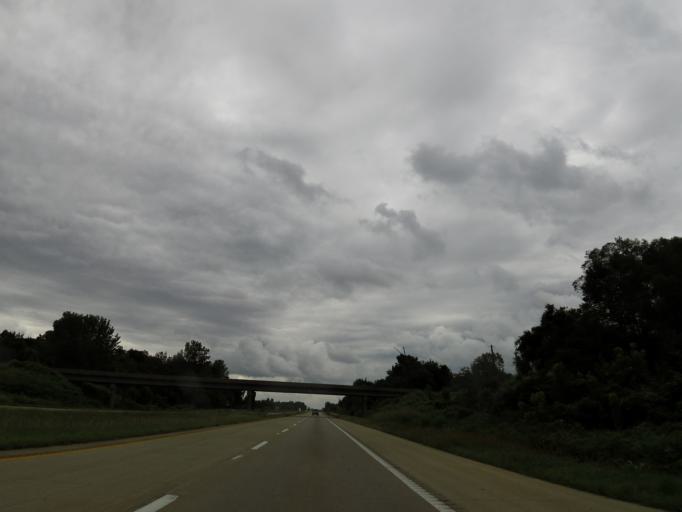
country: US
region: Missouri
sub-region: Mississippi County
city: Charleston
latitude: 36.9411
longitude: -89.2953
